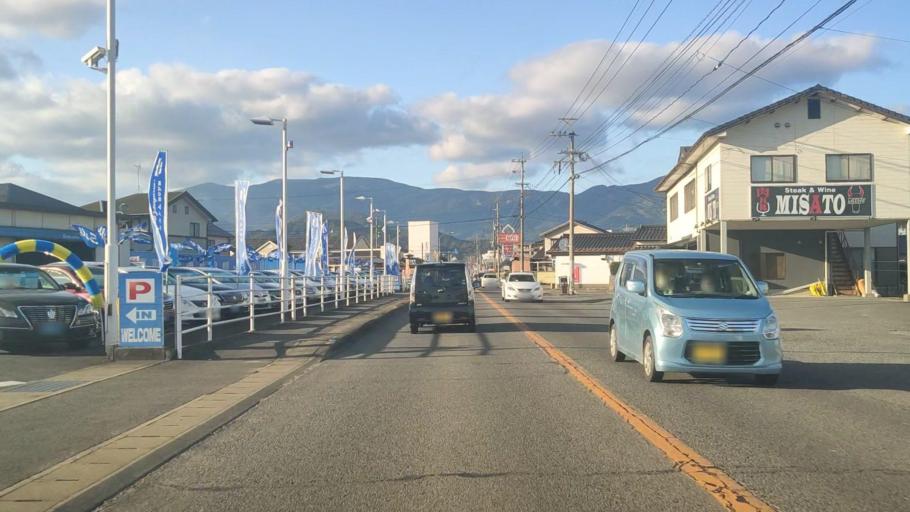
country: JP
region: Saga Prefecture
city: Saga-shi
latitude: 33.2854
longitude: 130.2086
